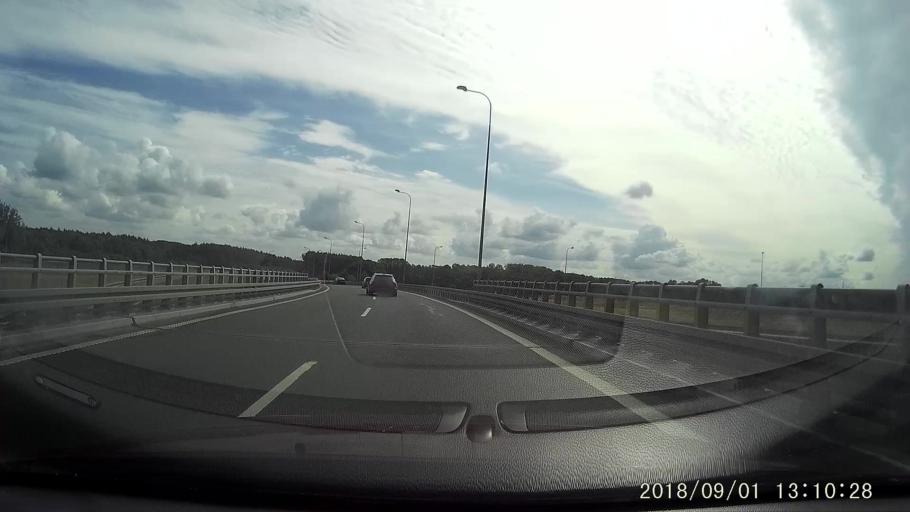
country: PL
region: West Pomeranian Voivodeship
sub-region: Szczecin
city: Szczecin
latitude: 53.3383
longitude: 14.5683
